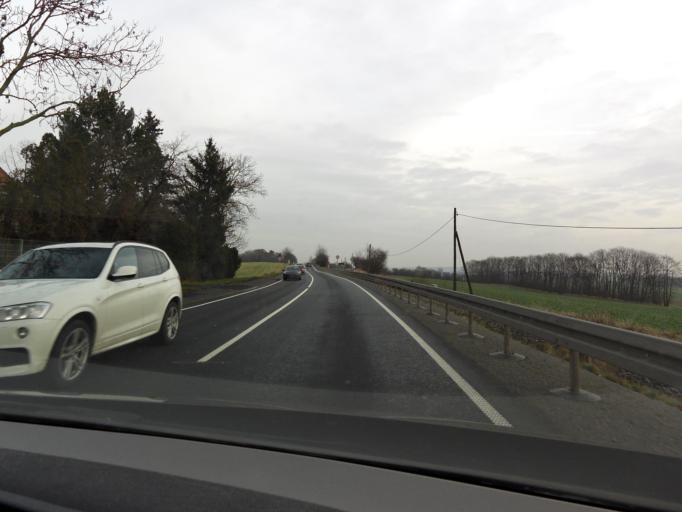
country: DE
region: Thuringia
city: Hopfgarten
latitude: 50.9708
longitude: 11.2689
